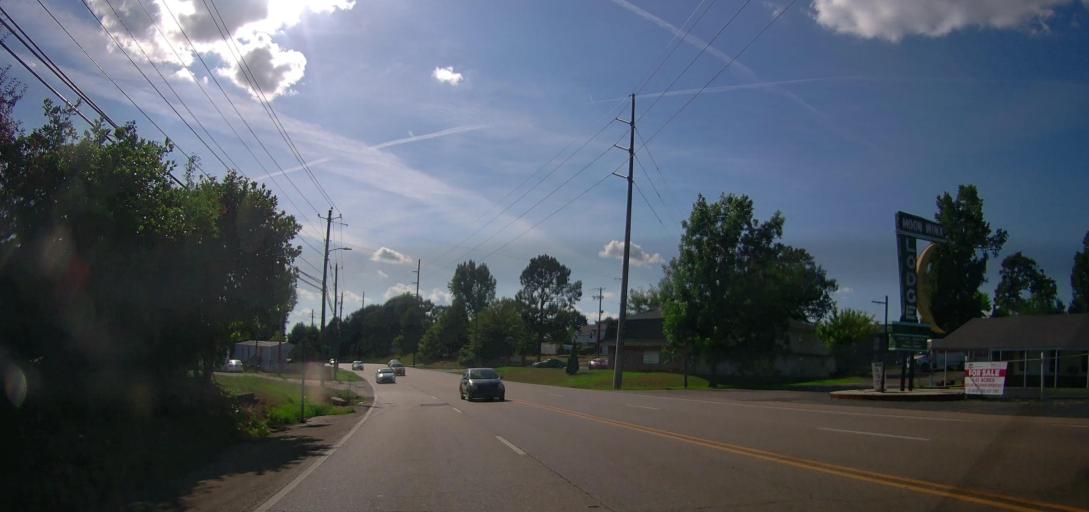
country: US
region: Alabama
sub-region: Tuscaloosa County
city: Holt
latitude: 33.2062
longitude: -87.4920
